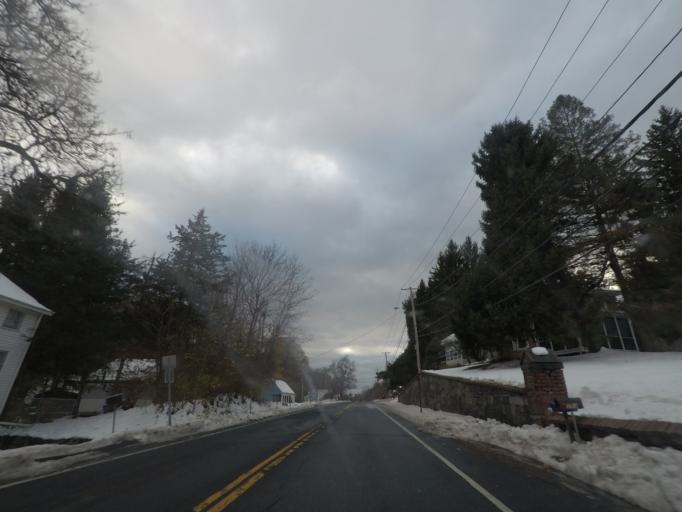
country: US
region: New York
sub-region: Ulster County
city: Kingston
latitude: 41.9130
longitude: -74.0184
